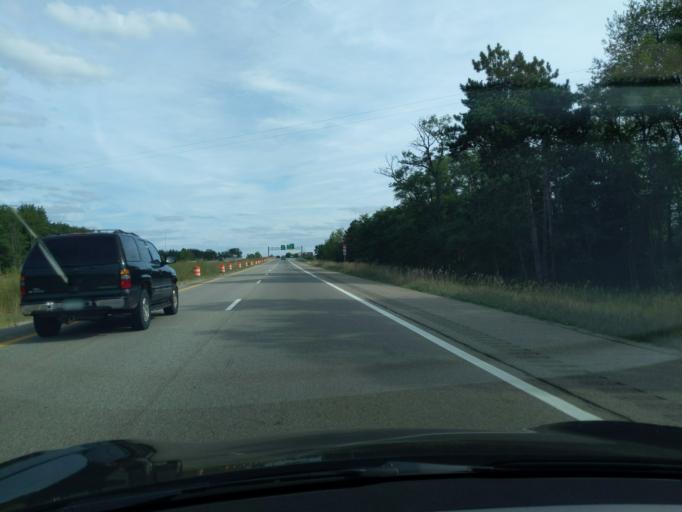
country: US
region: Michigan
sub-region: Muskegon County
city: Fruitport
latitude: 43.0821
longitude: -86.0893
